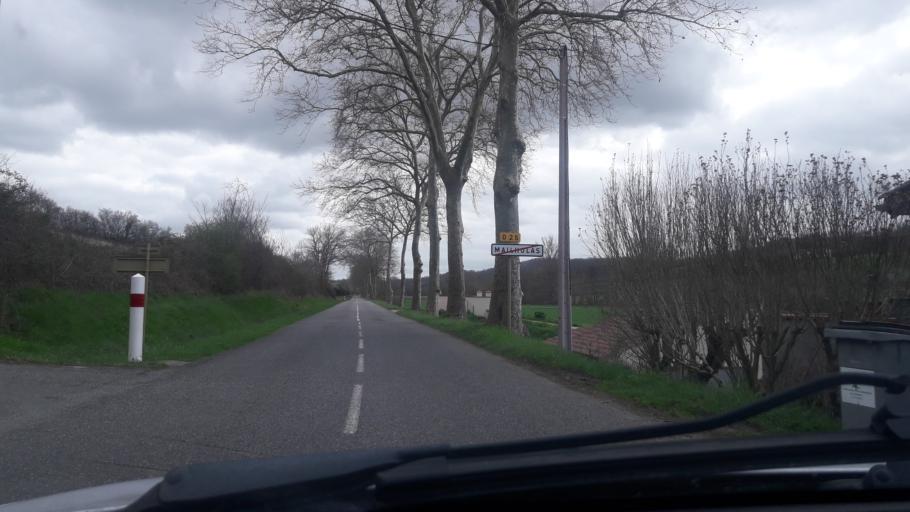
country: FR
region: Midi-Pyrenees
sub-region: Departement de la Haute-Garonne
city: Montesquieu-Volvestre
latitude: 43.2512
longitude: 1.2519
